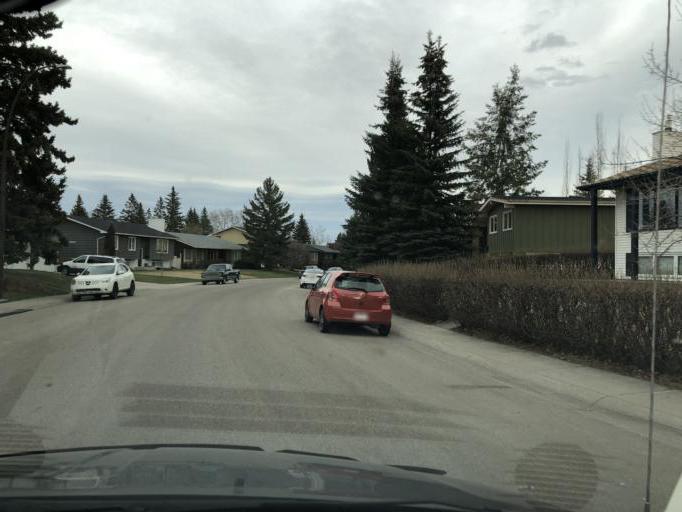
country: CA
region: Alberta
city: Calgary
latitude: 50.9325
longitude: -114.0435
